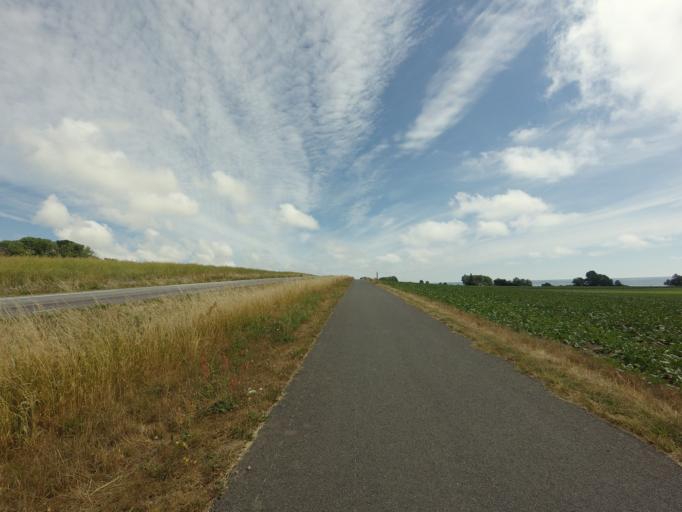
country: SE
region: Skane
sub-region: Simrishamns Kommun
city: Simrishamn
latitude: 55.4916
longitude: 14.3106
